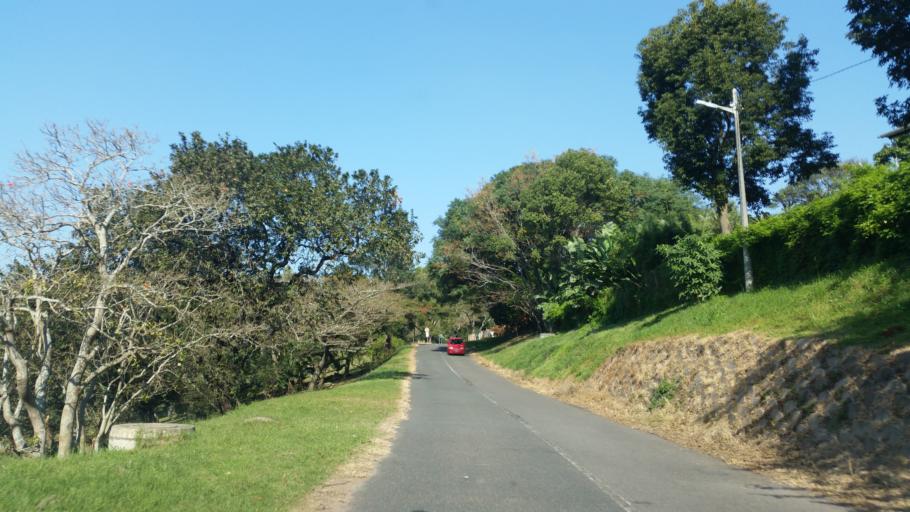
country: ZA
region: KwaZulu-Natal
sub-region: eThekwini Metropolitan Municipality
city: Berea
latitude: -29.8438
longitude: 30.9007
